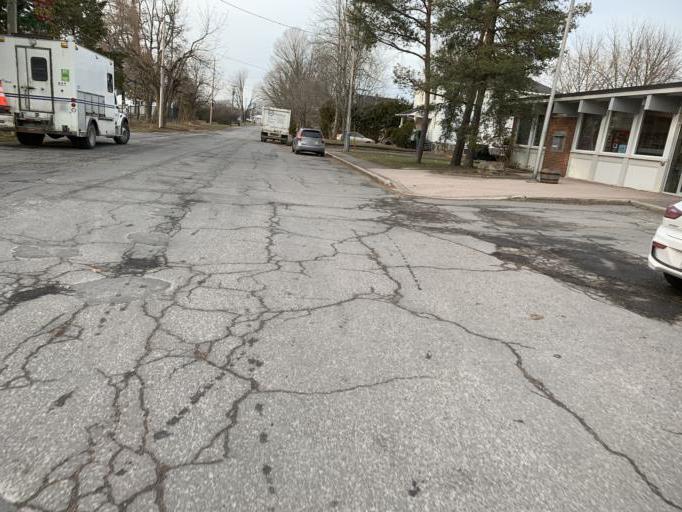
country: CA
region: Ontario
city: Bells Corners
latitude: 45.1925
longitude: -75.8341
